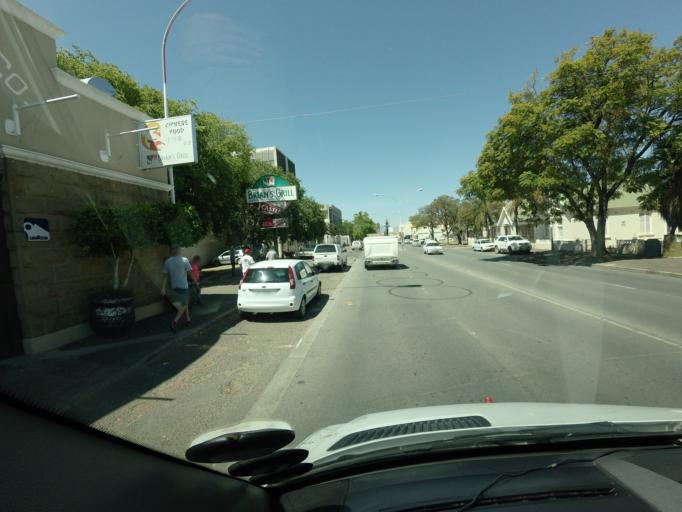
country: ZA
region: Western Cape
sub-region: Eden District Municipality
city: Oudtshoorn
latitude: -33.5892
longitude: 22.2032
